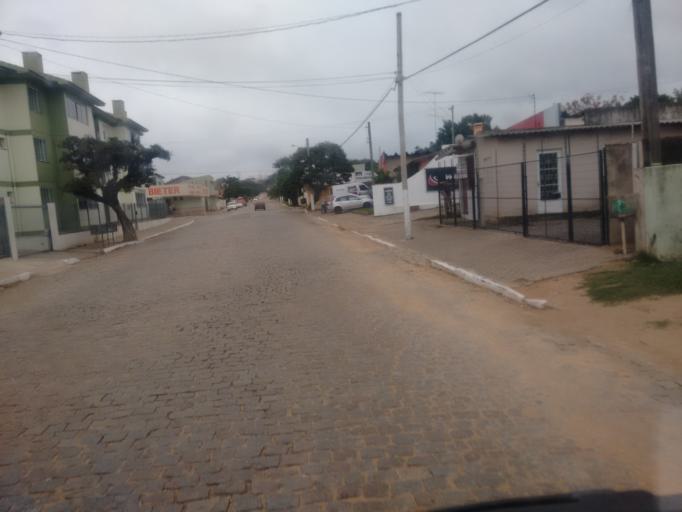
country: BR
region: Rio Grande do Sul
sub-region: Camaqua
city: Camaqua
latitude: -30.8395
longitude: -51.8152
